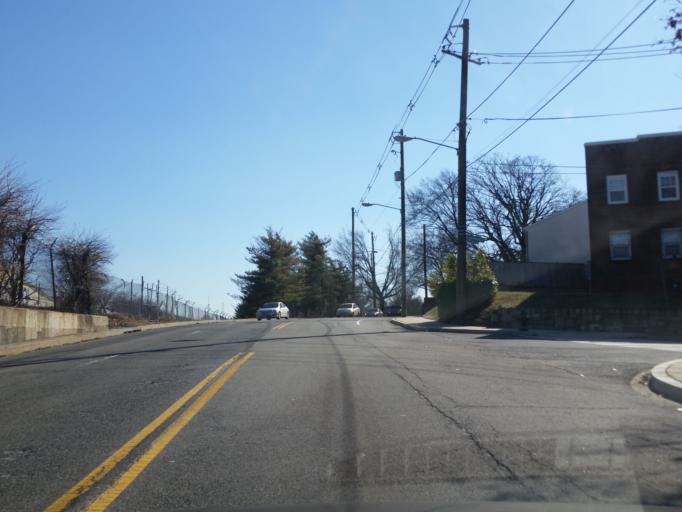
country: US
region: Maryland
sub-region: Montgomery County
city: Takoma Park
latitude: 38.9689
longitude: -77.0144
